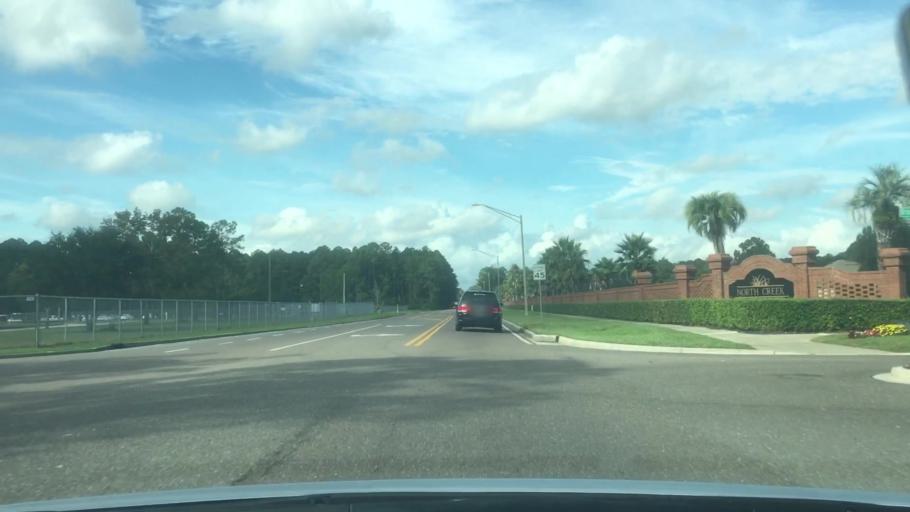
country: US
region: Florida
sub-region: Nassau County
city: Yulee
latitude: 30.4844
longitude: -81.6073
